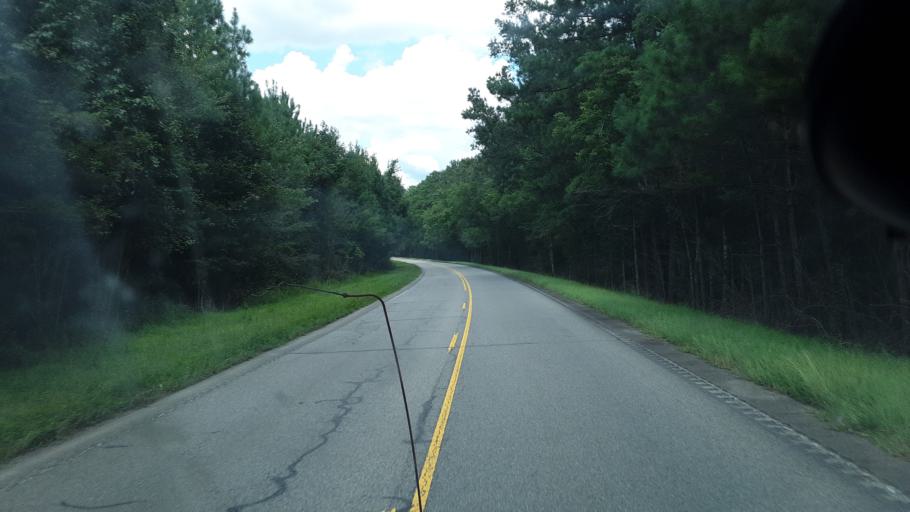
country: US
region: South Carolina
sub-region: Williamsburg County
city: Andrews
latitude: 33.5585
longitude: -79.4568
